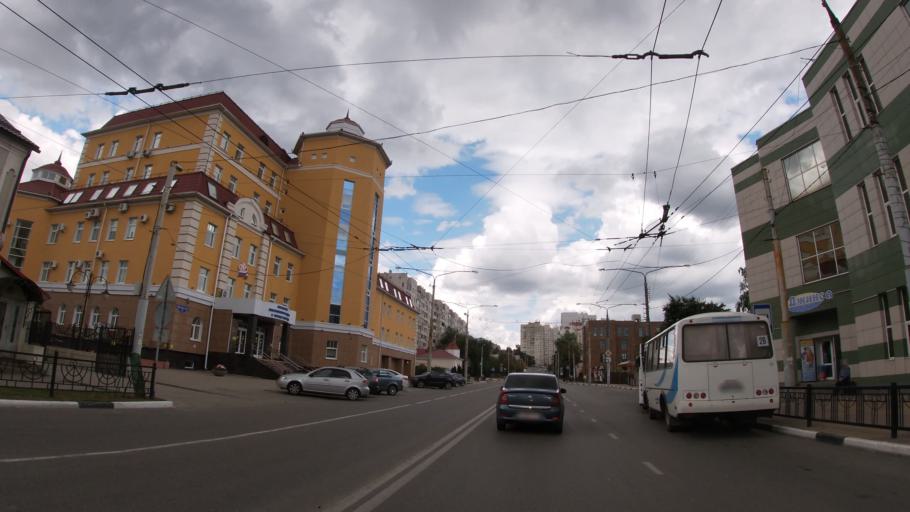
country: RU
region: Belgorod
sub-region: Belgorodskiy Rayon
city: Belgorod
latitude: 50.5953
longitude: 36.6058
